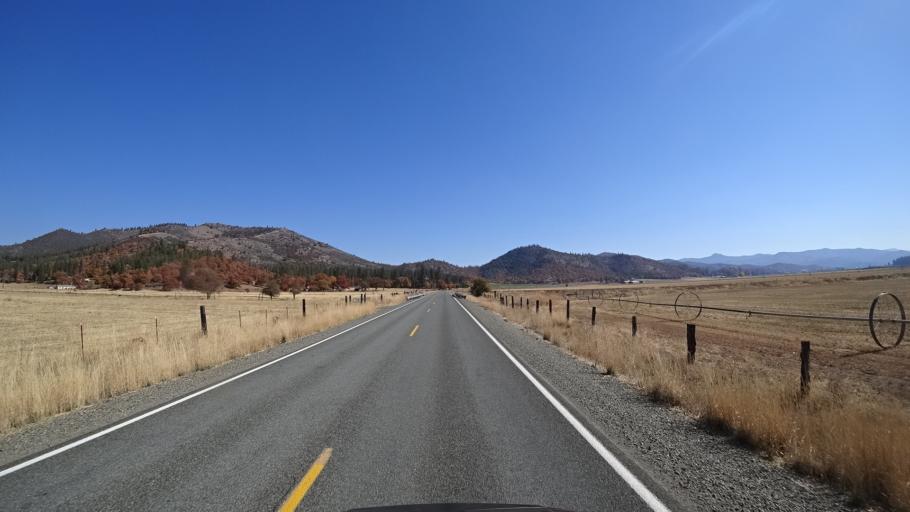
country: US
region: California
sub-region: Siskiyou County
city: Yreka
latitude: 41.6286
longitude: -122.8788
